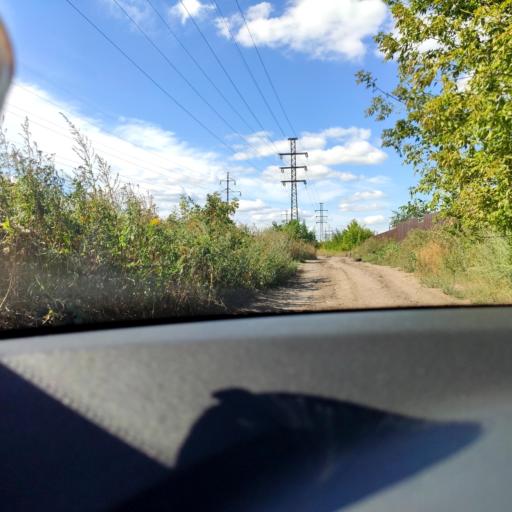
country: RU
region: Samara
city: Petra-Dubrava
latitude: 53.2906
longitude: 50.3080
